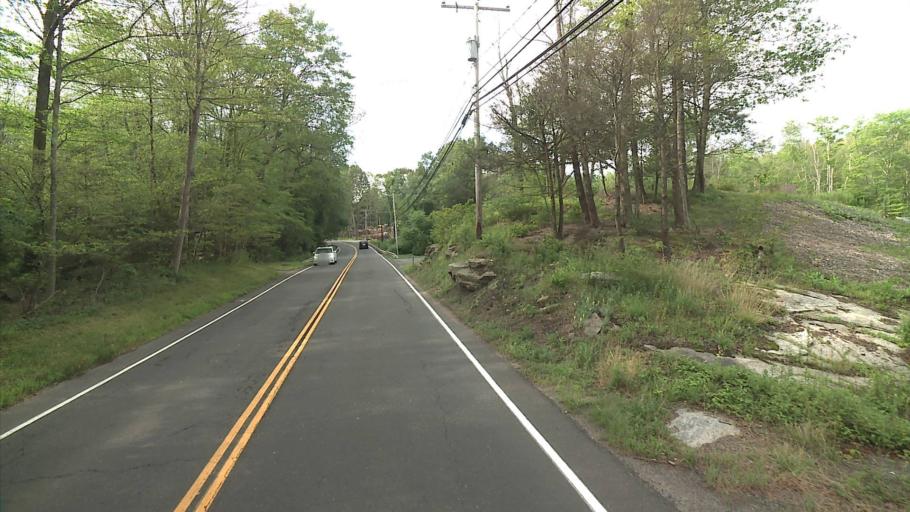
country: US
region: Connecticut
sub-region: Middlesex County
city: Higganum
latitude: 41.4678
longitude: -72.5577
